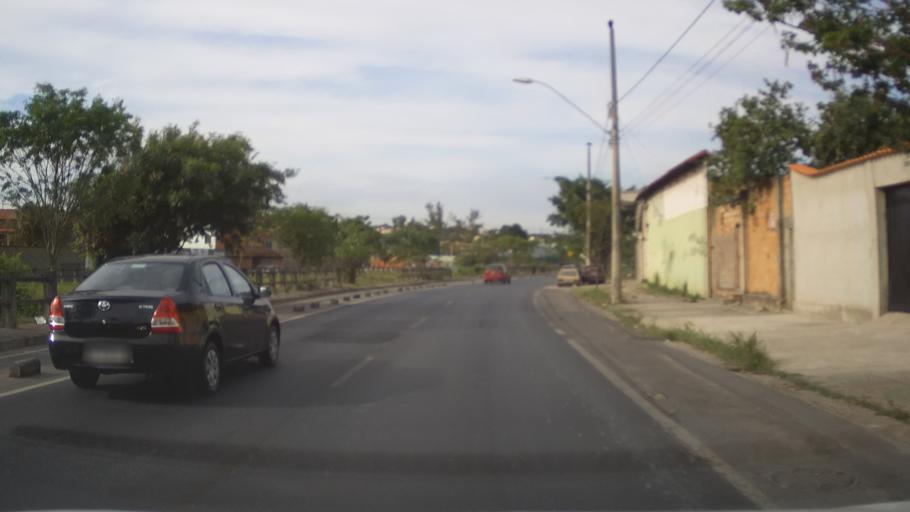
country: BR
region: Minas Gerais
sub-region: Contagem
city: Contagem
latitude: -19.8713
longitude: -44.0125
